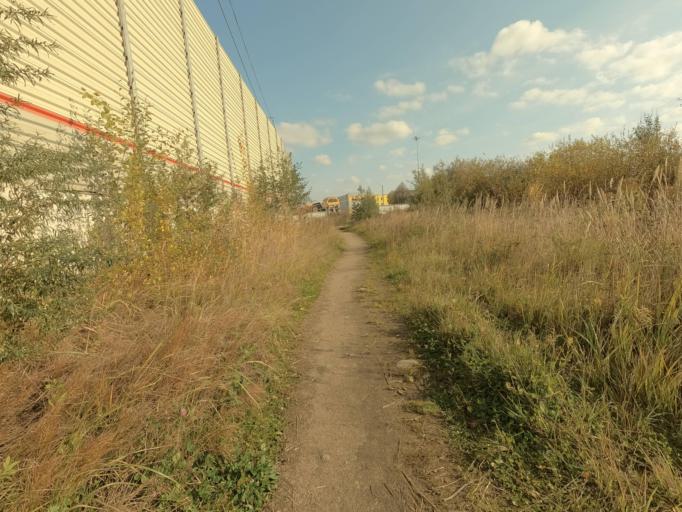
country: RU
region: Leningrad
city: Mga
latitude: 59.7542
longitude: 31.0713
